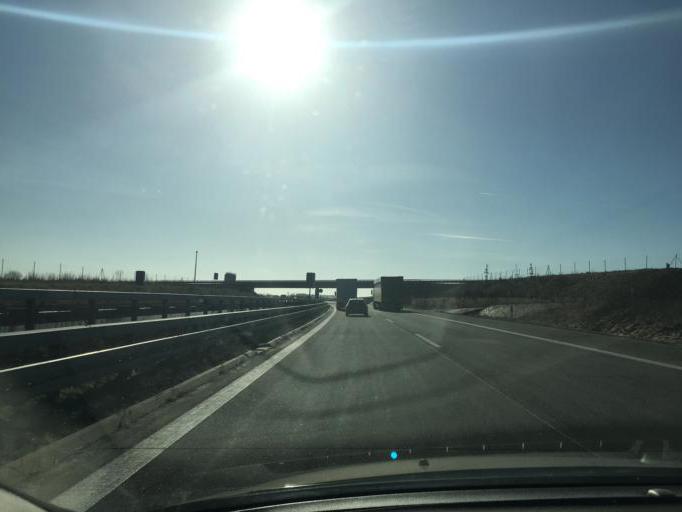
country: DE
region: Saxony
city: Geithain
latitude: 51.0499
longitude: 12.6334
